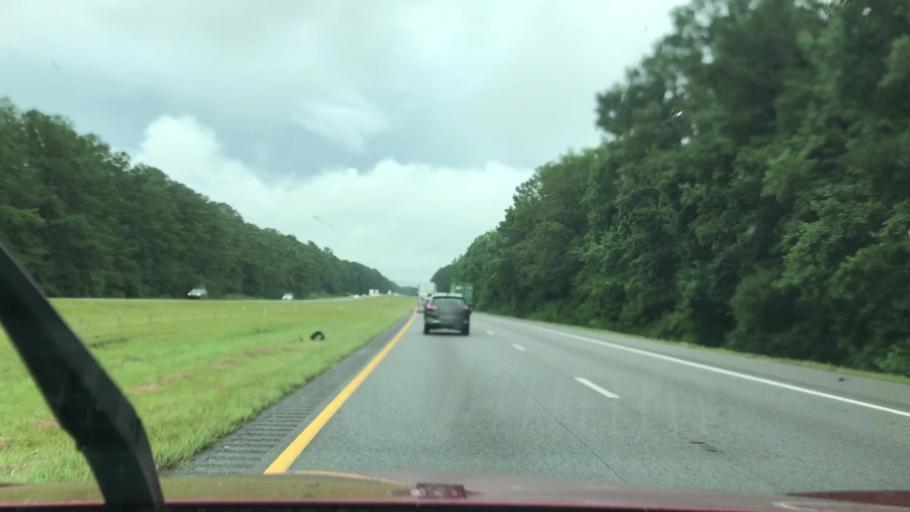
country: US
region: South Carolina
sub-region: Dorchester County
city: Ridgeville
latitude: 33.0920
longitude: -80.2282
